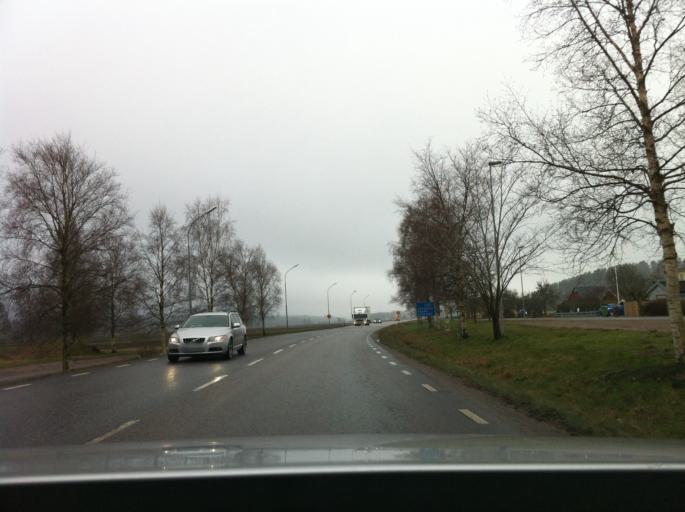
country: SE
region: Vaestra Goetaland
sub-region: Alingsas Kommun
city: Sollebrunn
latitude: 58.1169
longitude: 12.5326
